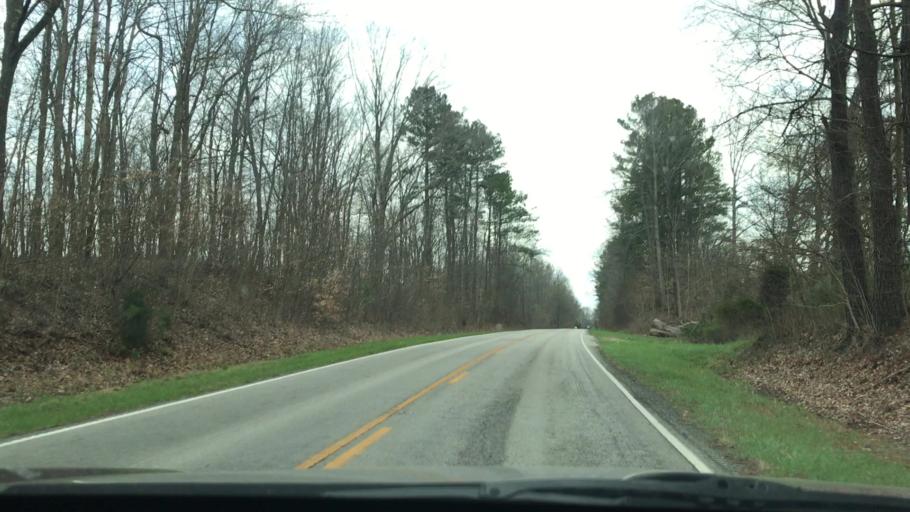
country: US
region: Kentucky
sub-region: Hart County
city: Munfordville
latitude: 37.3103
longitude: -85.7623
